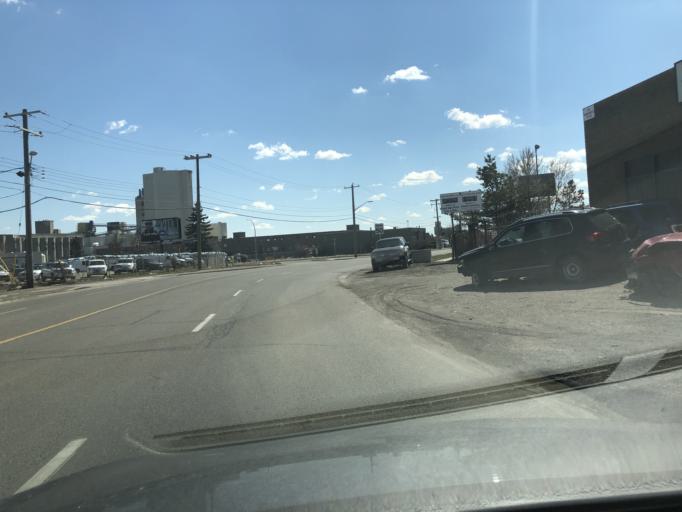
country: CA
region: Alberta
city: Calgary
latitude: 51.0292
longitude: -114.0313
